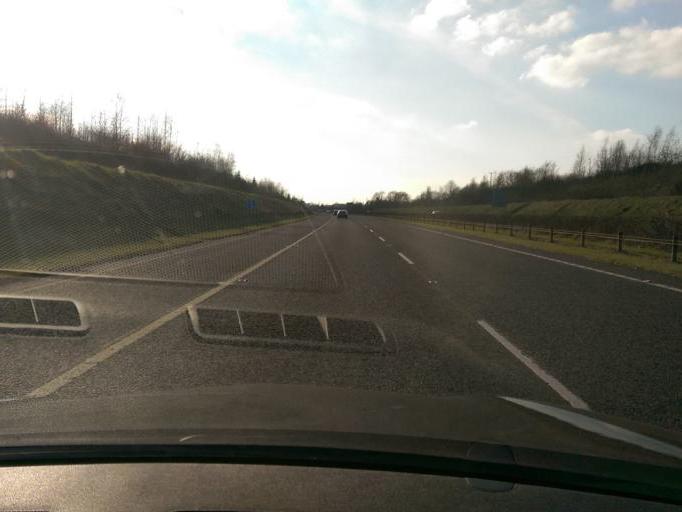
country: IE
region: Leinster
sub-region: Kildare
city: Kildare
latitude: 53.1543
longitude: -6.9376
